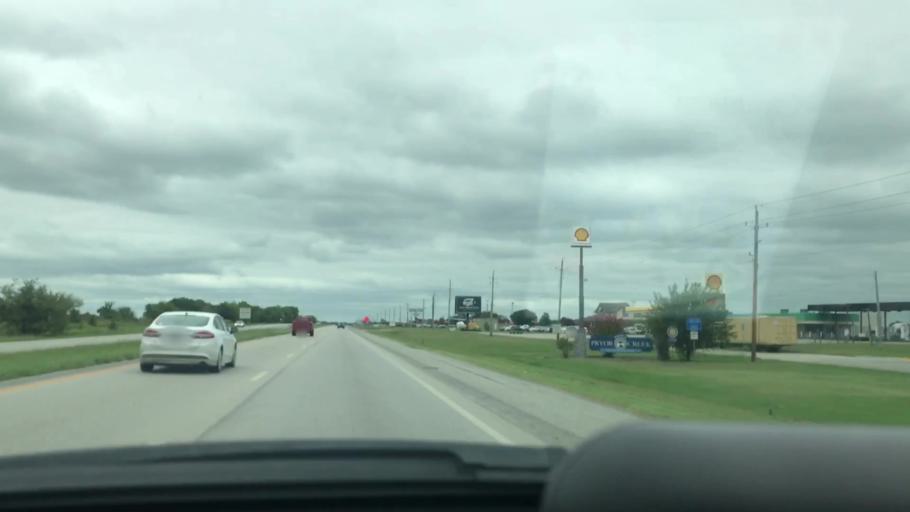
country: US
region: Oklahoma
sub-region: Mayes County
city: Pryor
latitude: 36.2498
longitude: -95.3364
